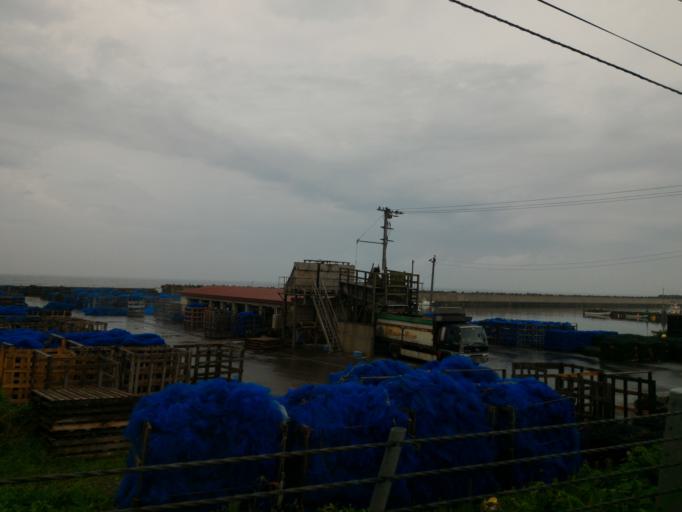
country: JP
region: Hokkaido
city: Rumoi
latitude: 43.9944
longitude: 141.6516
